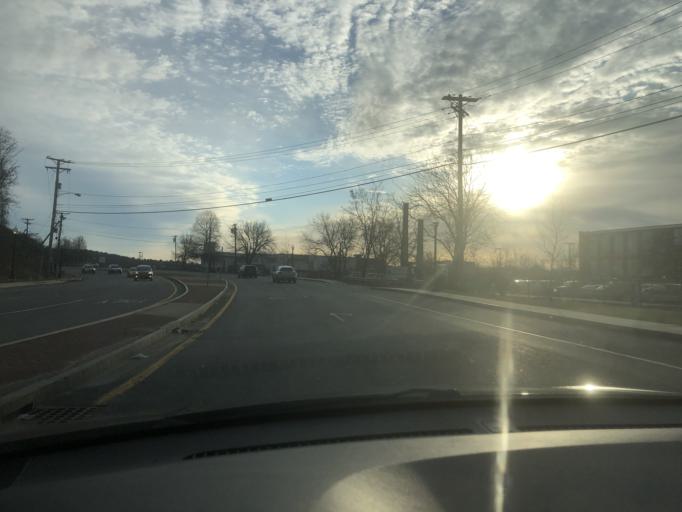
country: US
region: Massachusetts
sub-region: Essex County
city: North Andover
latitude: 42.7073
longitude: -71.1460
